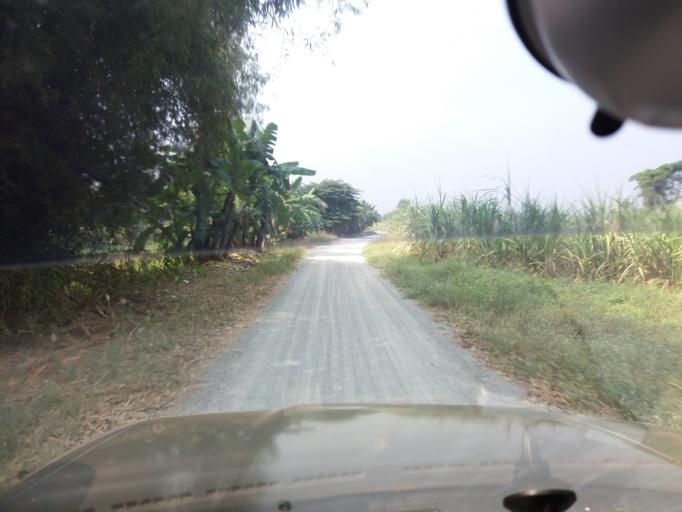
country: TH
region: Sing Buri
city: Bang Racham
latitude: 14.8975
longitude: 100.2101
